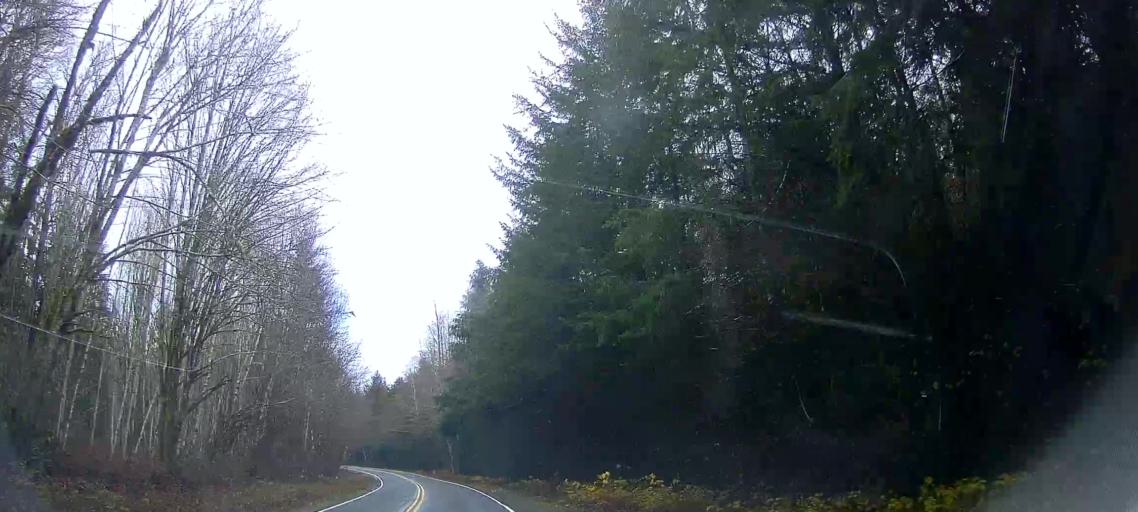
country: US
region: Washington
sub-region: Snohomish County
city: Darrington
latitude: 48.4901
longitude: -121.4765
